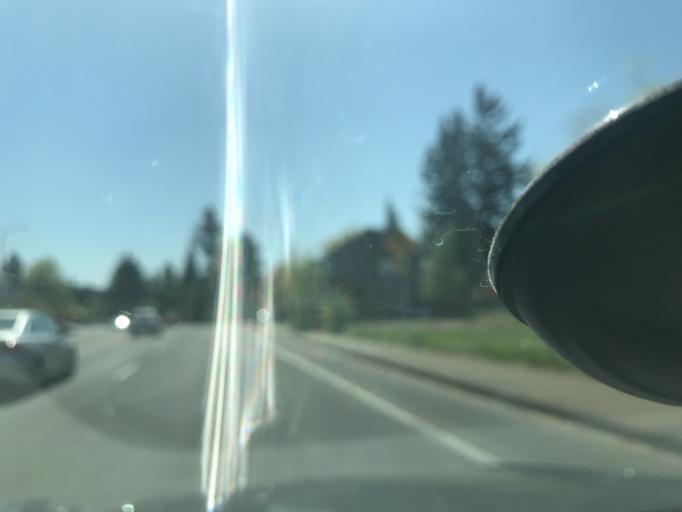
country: US
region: Oregon
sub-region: Multnomah County
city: Fairview
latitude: 45.5175
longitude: -122.4770
